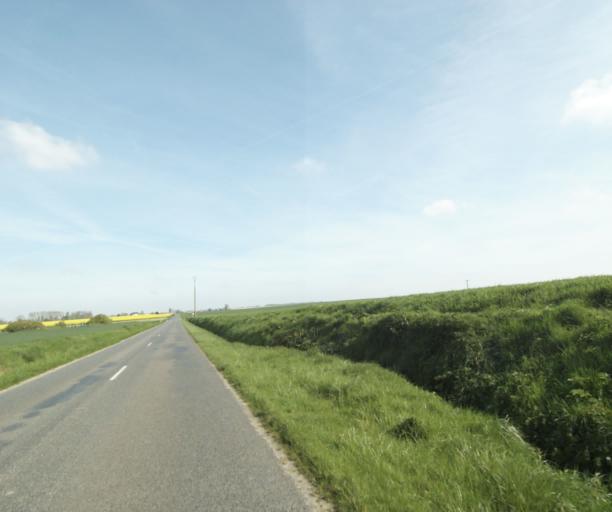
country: FR
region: Ile-de-France
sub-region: Departement de Seine-et-Marne
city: Nangis
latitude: 48.5694
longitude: 3.0125
